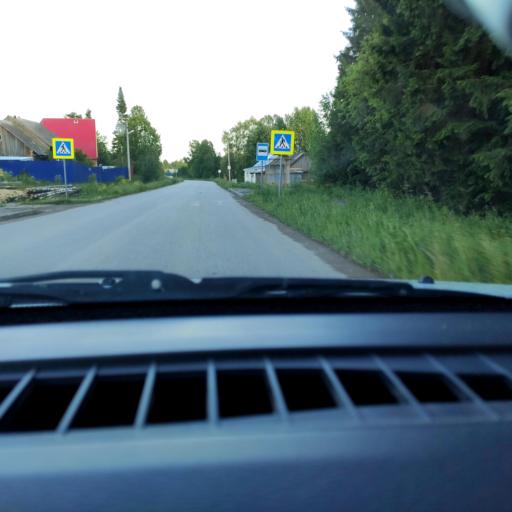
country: RU
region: Perm
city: Polazna
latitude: 58.2104
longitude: 56.5132
